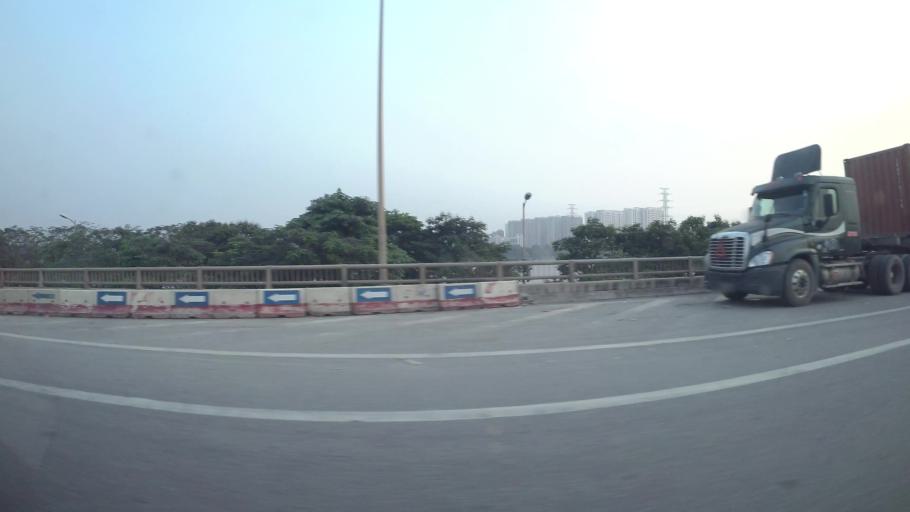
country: VN
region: Ha Noi
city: Van Dien
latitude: 20.9655
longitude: 105.8522
